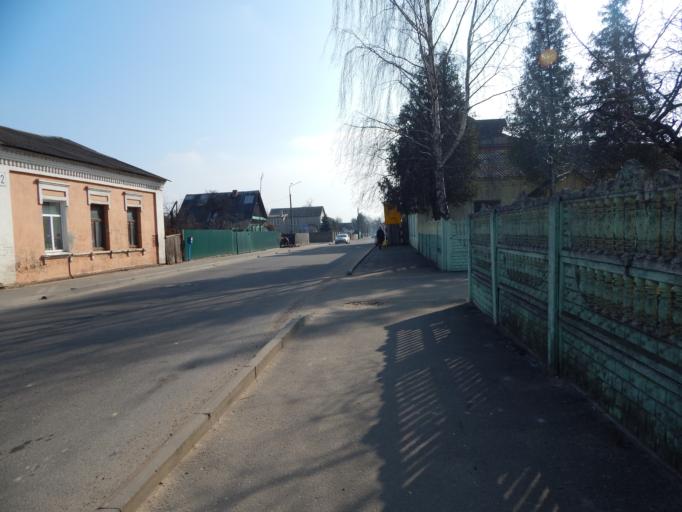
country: BY
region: Minsk
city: Horad Barysaw
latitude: 54.2460
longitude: 28.5083
